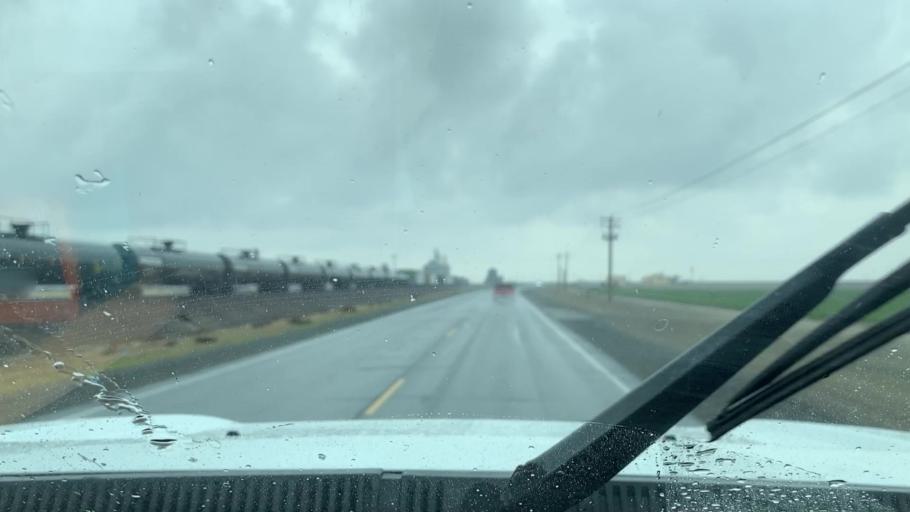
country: US
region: California
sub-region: Tulare County
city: Alpaugh
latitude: 35.9832
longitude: -119.4723
